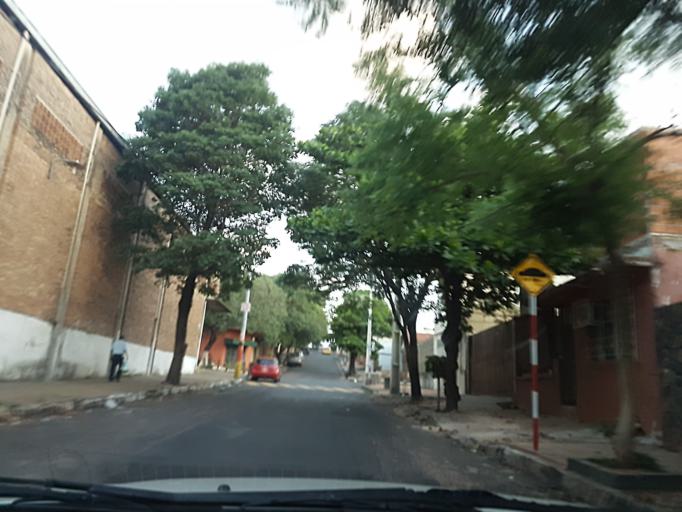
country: PY
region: Asuncion
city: Asuncion
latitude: -25.2980
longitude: -57.6158
